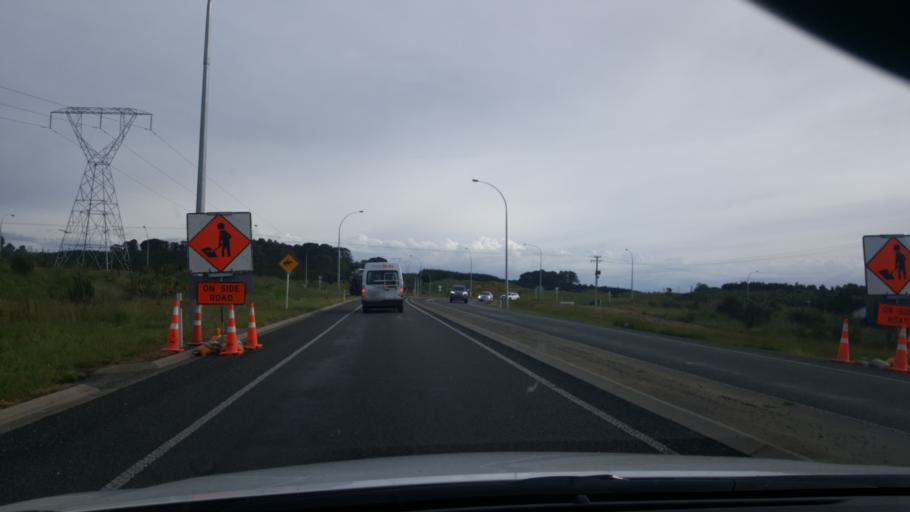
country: NZ
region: Waikato
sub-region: Taupo District
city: Taupo
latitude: -38.7030
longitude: 176.1119
